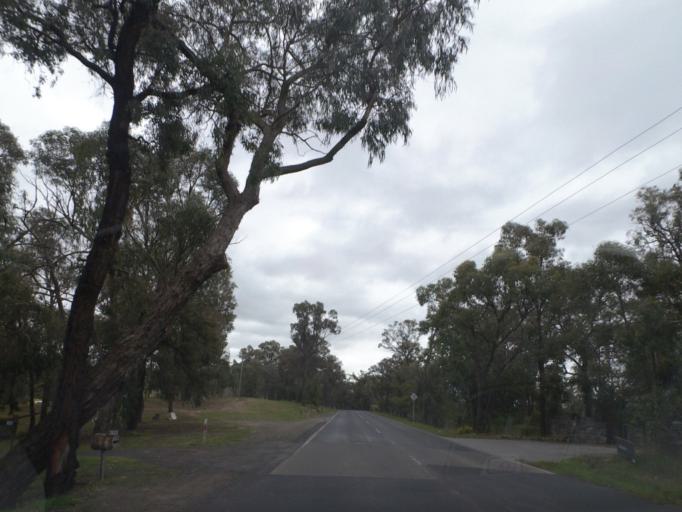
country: AU
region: Victoria
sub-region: Nillumbik
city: Diamond Creek
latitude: -37.6473
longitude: 145.1476
